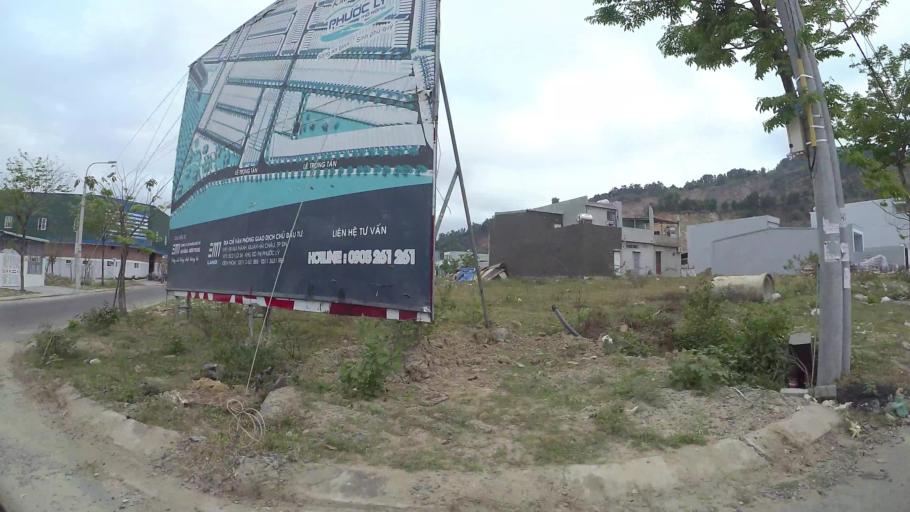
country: VN
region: Da Nang
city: Lien Chieu
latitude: 16.0438
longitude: 108.1673
